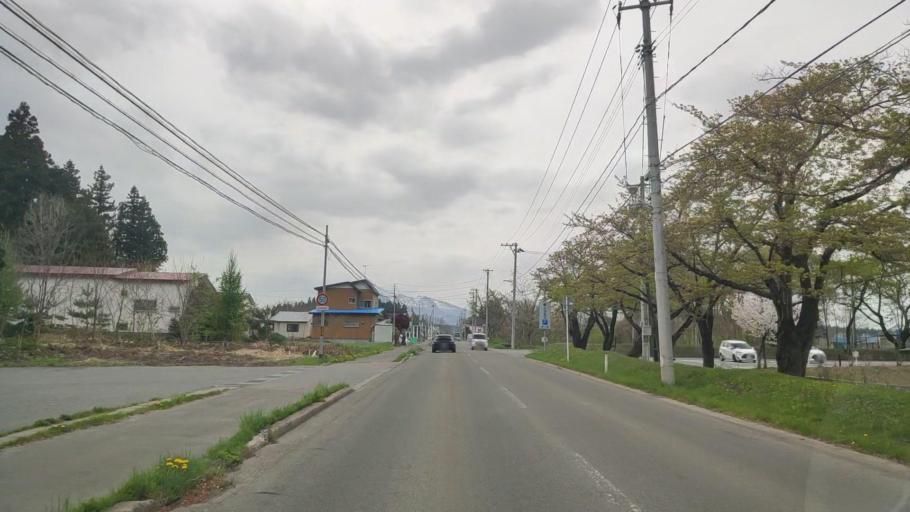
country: JP
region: Aomori
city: Aomori Shi
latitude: 40.7848
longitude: 140.7901
